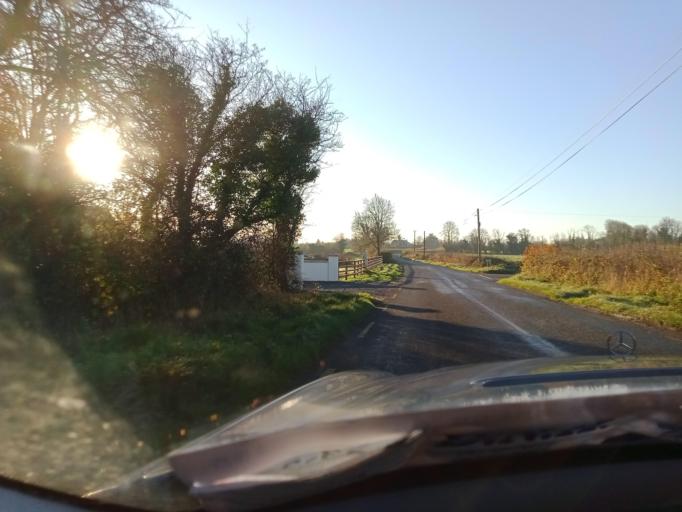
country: IE
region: Leinster
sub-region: Kilkenny
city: Callan
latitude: 52.5270
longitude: -7.3822
